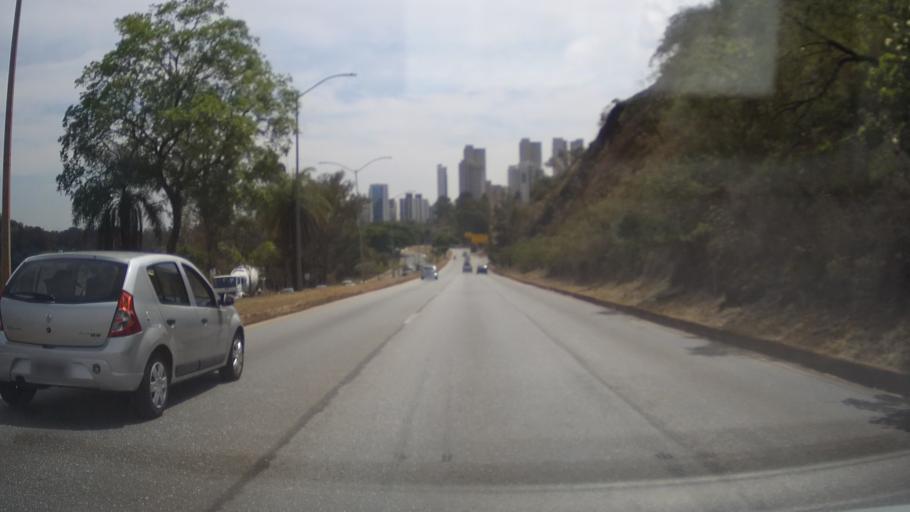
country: BR
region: Minas Gerais
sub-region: Belo Horizonte
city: Belo Horizonte
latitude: -19.9850
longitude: -43.9521
